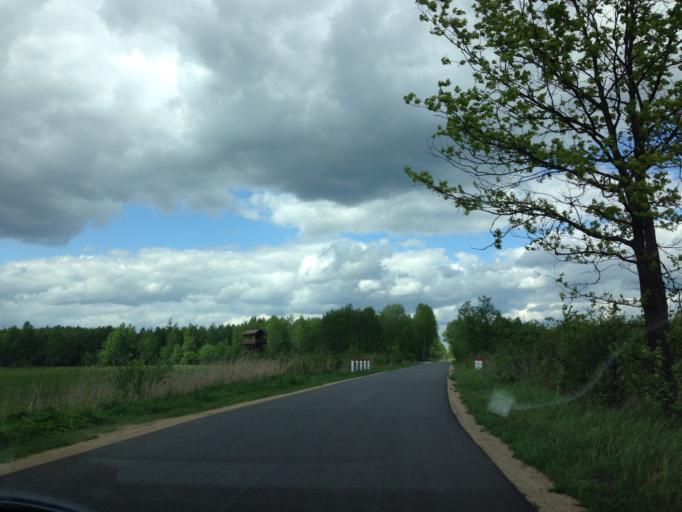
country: PL
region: Podlasie
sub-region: Powiat bialostocki
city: Tykocin
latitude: 53.2981
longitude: 22.6051
